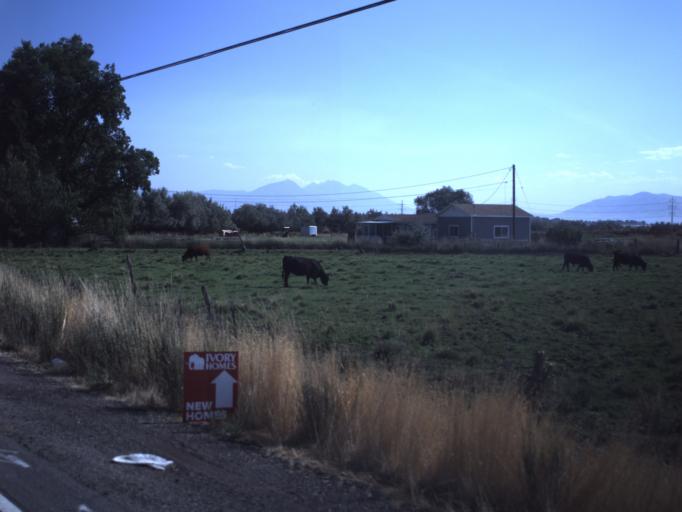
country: US
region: Utah
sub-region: Utah County
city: Orem
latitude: 40.2702
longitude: -111.7232
